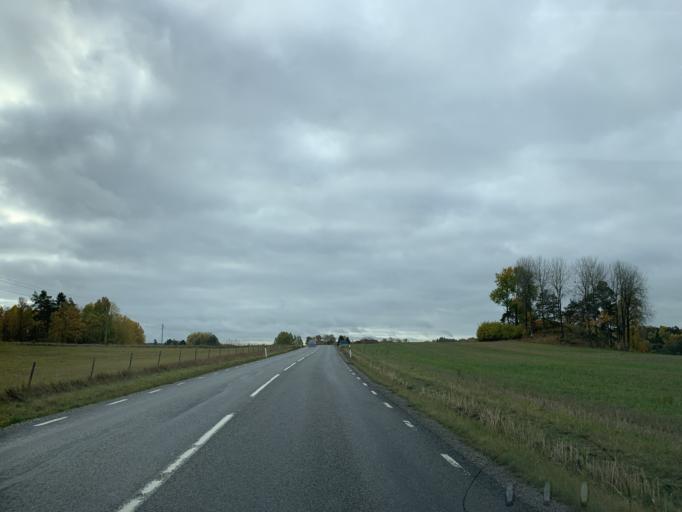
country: SE
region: Stockholm
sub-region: Nynashamns Kommun
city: Osmo
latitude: 59.0481
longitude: 17.8073
